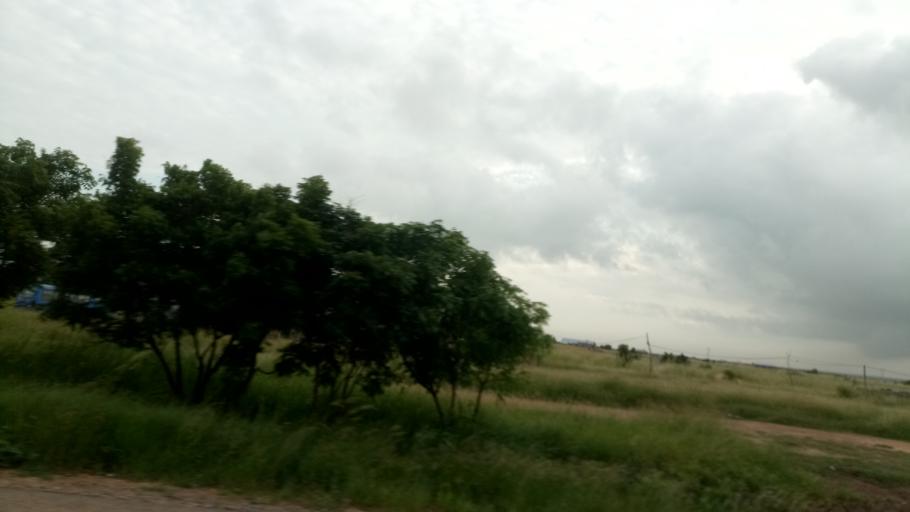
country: GH
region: Greater Accra
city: Tema
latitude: 5.8725
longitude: 0.3421
